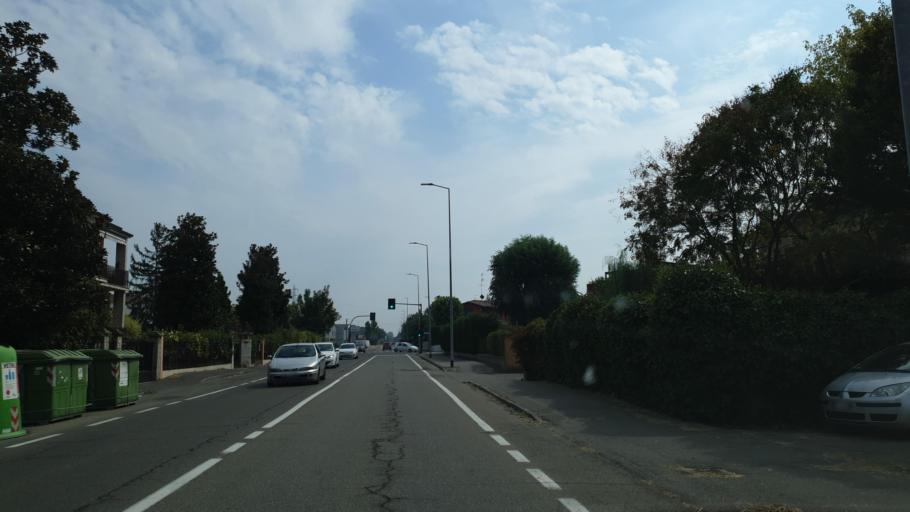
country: IT
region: Emilia-Romagna
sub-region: Provincia di Parma
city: Baganzola
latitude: 44.8242
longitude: 10.2806
